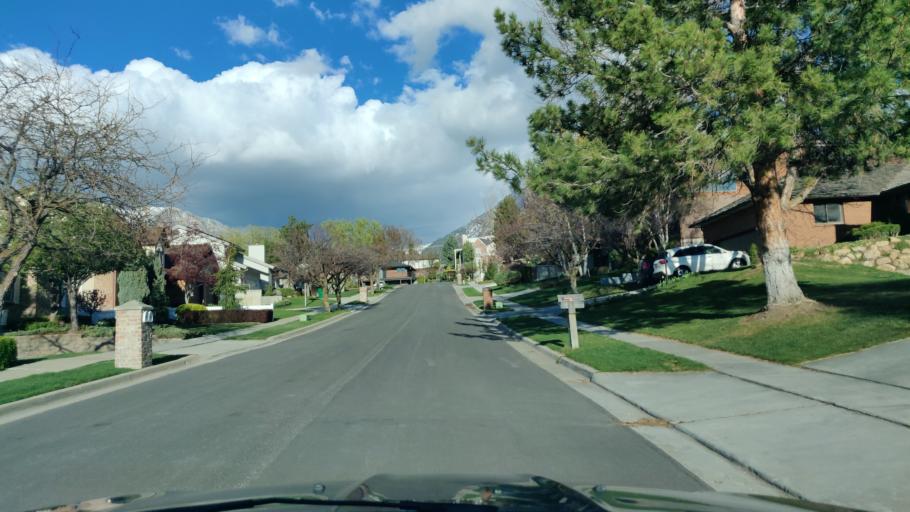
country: US
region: Utah
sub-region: Salt Lake County
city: Little Cottonwood Creek Valley
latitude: 40.6171
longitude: -111.8273
